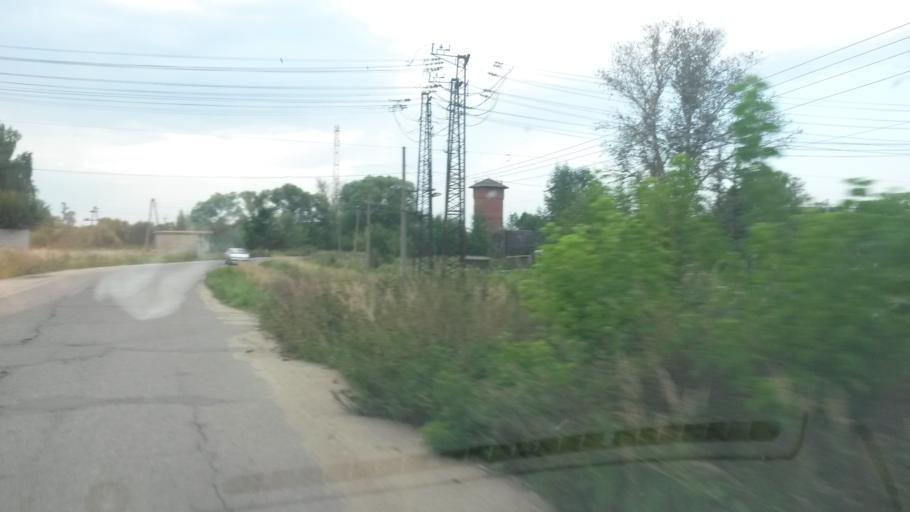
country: RU
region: Jaroslavl
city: Petrovsk
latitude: 56.9989
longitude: 39.2702
